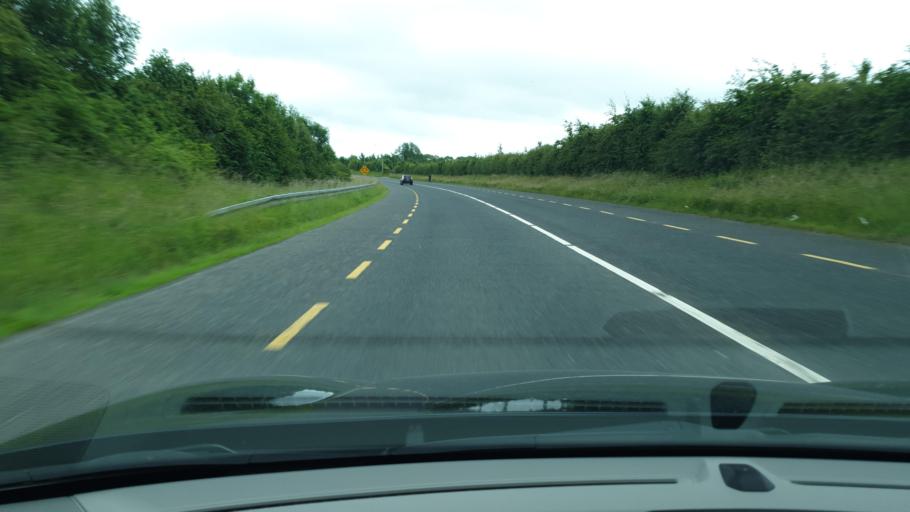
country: IE
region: Leinster
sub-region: An Mhi
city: Dunshaughlin
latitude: 53.5128
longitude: -6.5573
